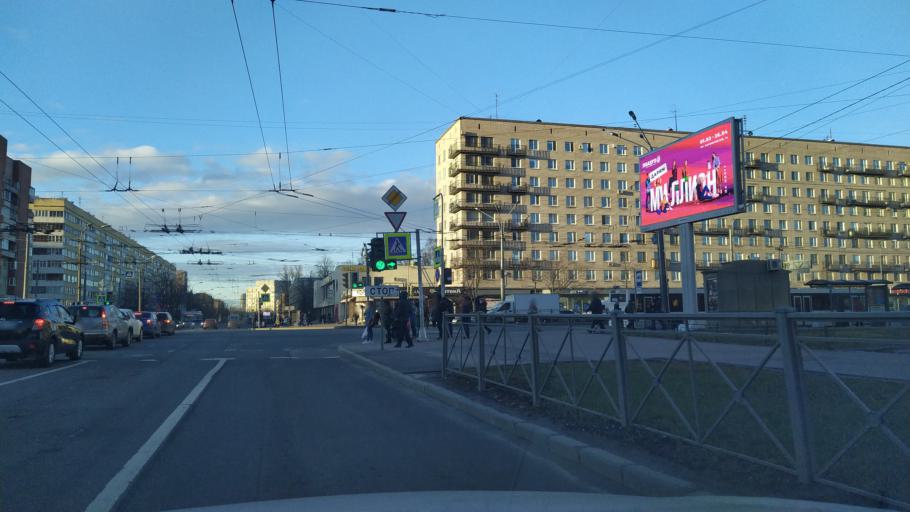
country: RU
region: St.-Petersburg
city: Dachnoye
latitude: 59.8515
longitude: 30.2564
